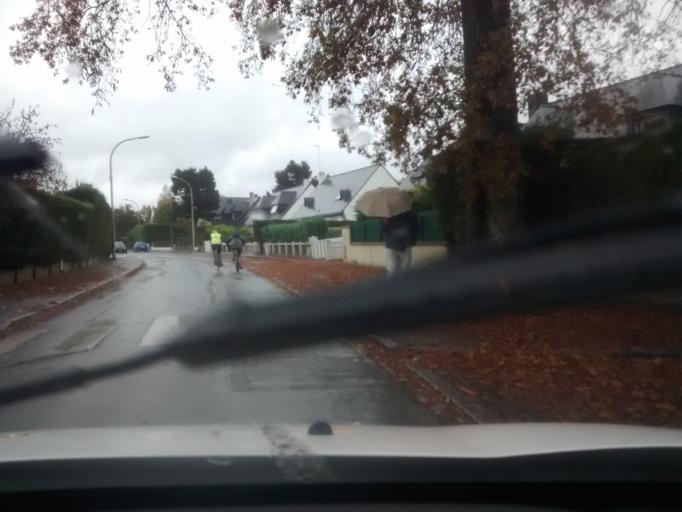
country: FR
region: Brittany
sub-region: Departement d'Ille-et-Vilaine
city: Fouillard
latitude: 48.1571
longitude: -1.5800
